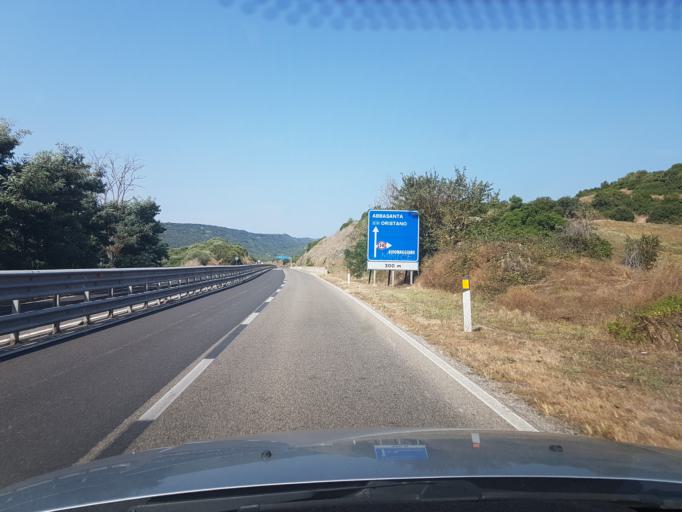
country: IT
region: Sardinia
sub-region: Provincia di Oristano
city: Soddi
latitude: 40.1487
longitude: 8.8882
